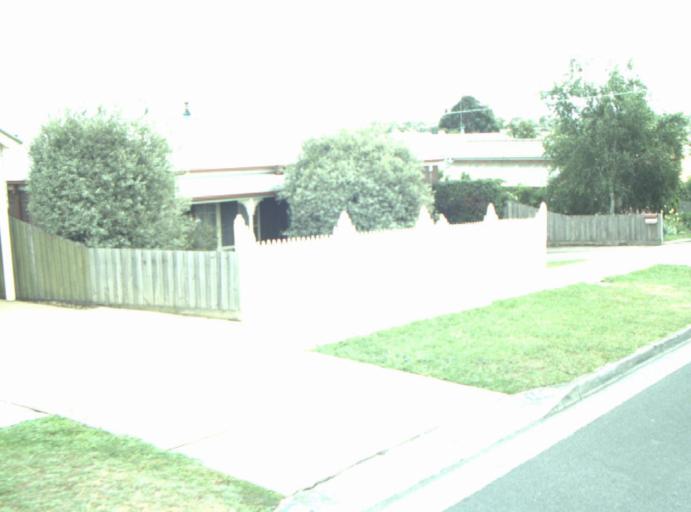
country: AU
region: Victoria
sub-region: Greater Geelong
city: Wandana Heights
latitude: -38.2005
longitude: 144.3269
